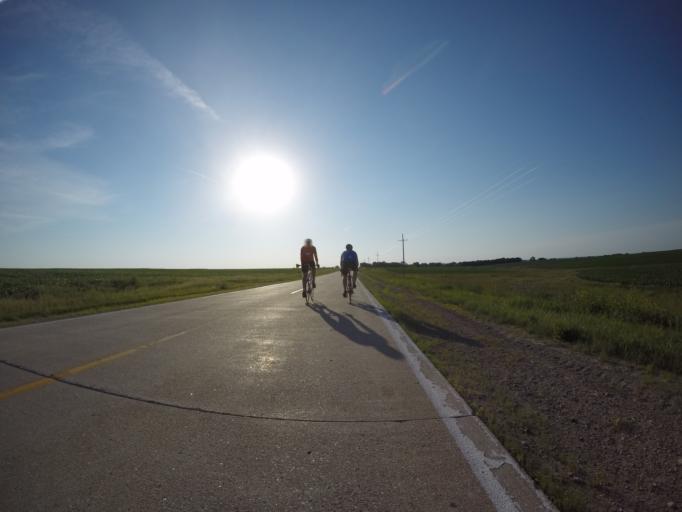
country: US
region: Nebraska
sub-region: Gage County
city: Wymore
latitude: 40.0448
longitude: -96.6124
